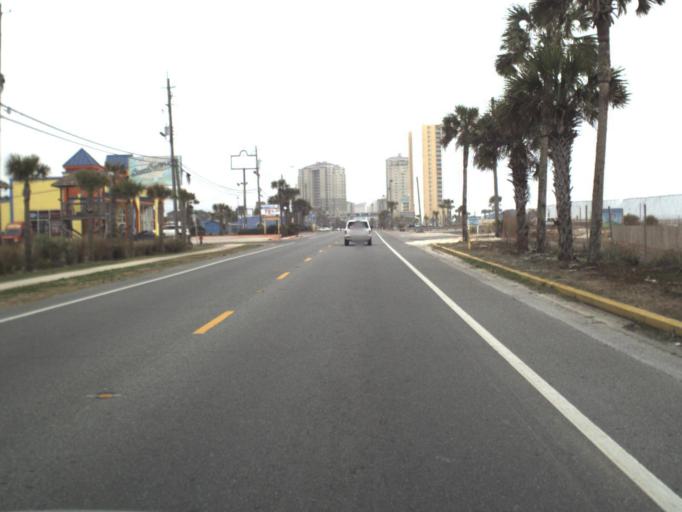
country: US
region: Florida
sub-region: Bay County
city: Panama City Beach
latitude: 30.1923
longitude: -85.8336
